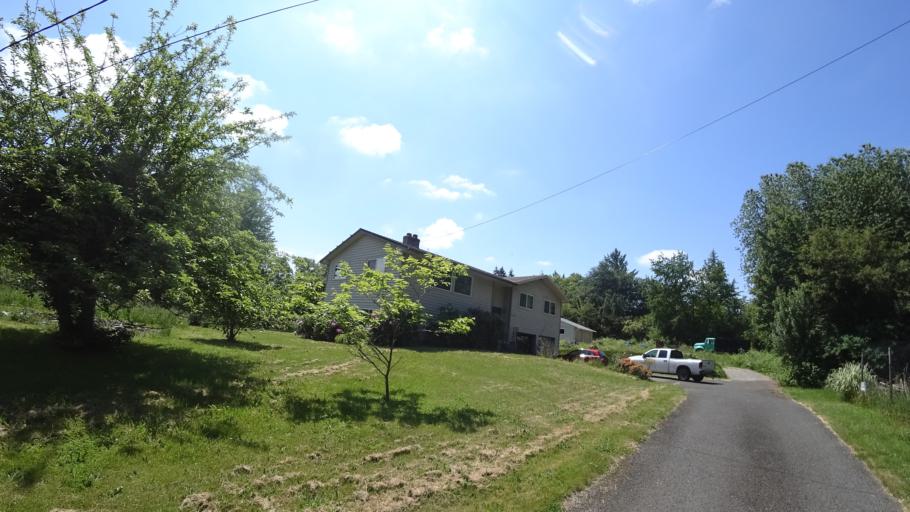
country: US
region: Oregon
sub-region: Clackamas County
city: Lake Oswego
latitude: 45.4376
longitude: -122.6983
